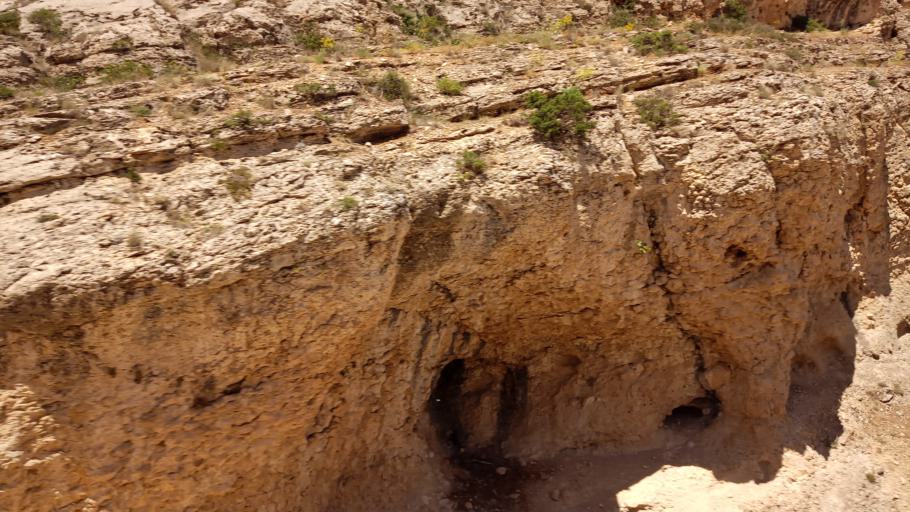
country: TR
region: Malatya
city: Darende
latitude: 38.5745
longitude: 37.4629
